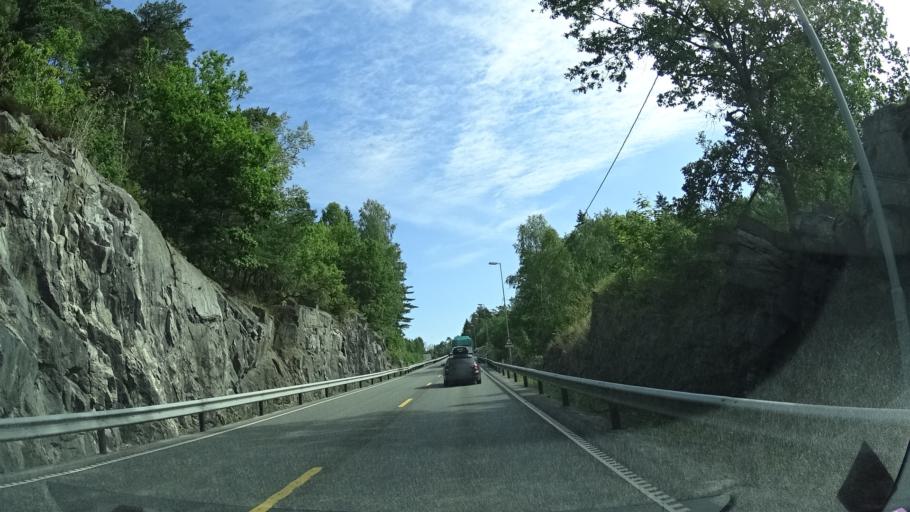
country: NO
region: Telemark
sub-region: Bamble
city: Langesund
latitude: 58.9944
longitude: 9.6424
